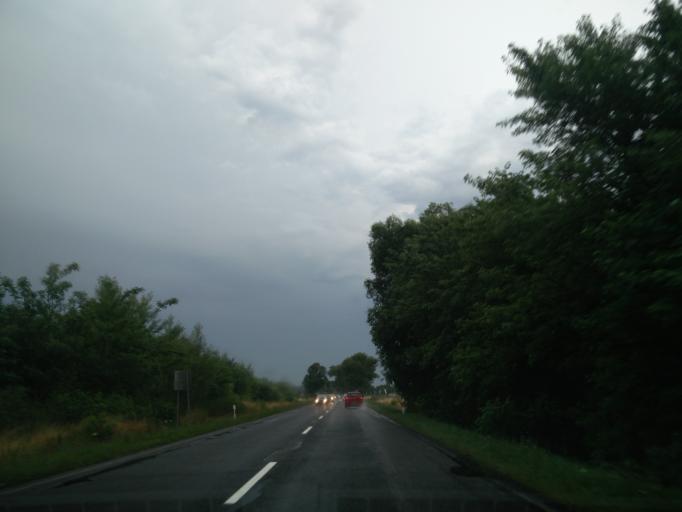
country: HU
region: Veszprem
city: Devecser
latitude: 47.1267
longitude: 17.3635
